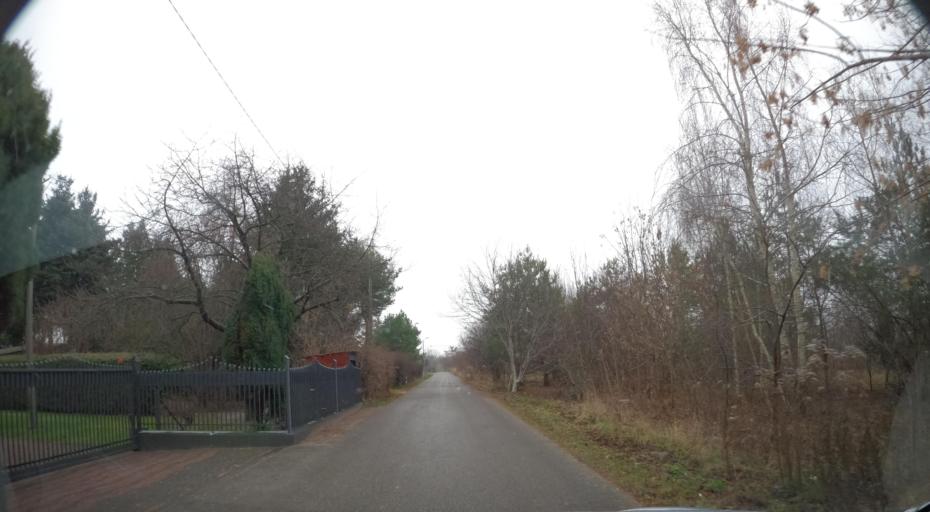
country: PL
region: Masovian Voivodeship
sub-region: Powiat radomski
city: Jastrzebia
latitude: 51.4319
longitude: 21.2295
